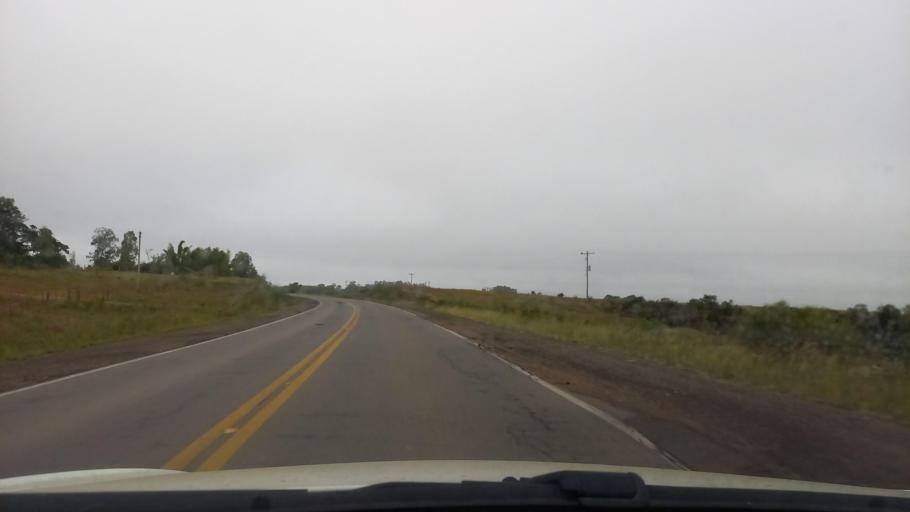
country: BR
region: Rio Grande do Sul
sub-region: Rosario Do Sul
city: Rosario do Sul
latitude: -30.1261
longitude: -54.6540
